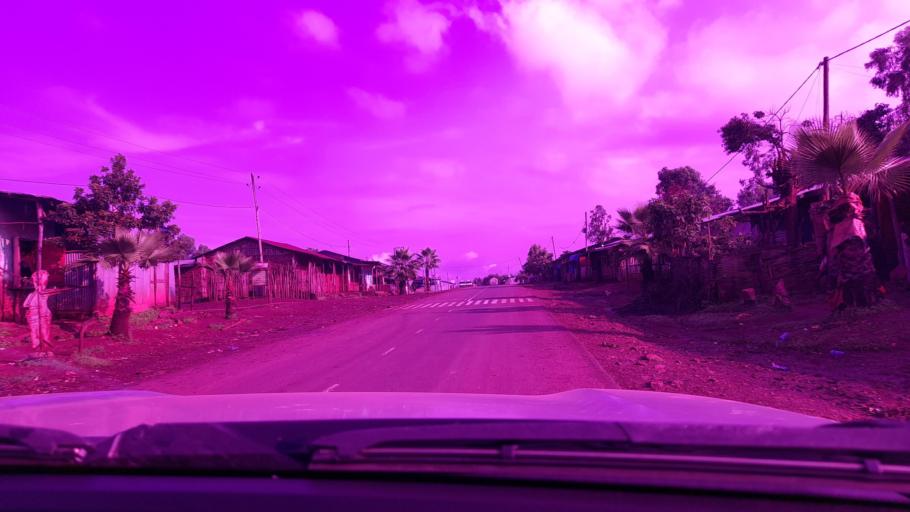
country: ET
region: Oromiya
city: Bedele
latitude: 8.1744
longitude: 36.4591
